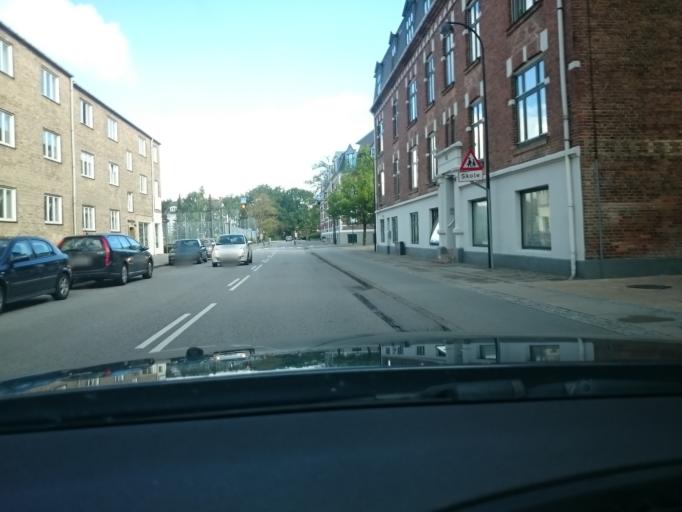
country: DK
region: Capital Region
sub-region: Gentofte Kommune
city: Charlottenlund
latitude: 55.7579
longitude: 12.5756
